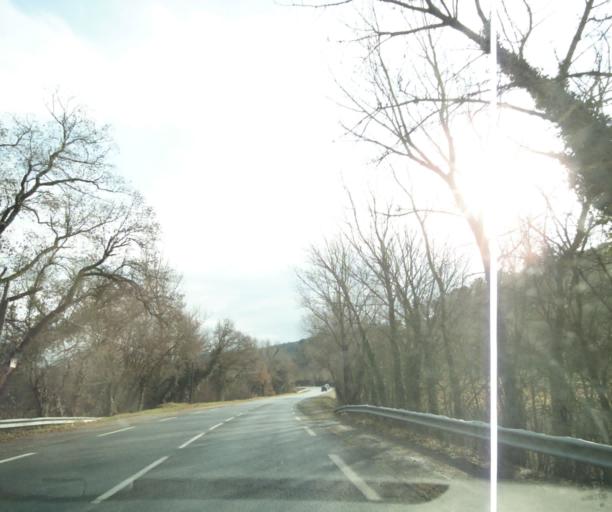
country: FR
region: Provence-Alpes-Cote d'Azur
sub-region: Departement du Var
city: Tourves
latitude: 43.4034
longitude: 5.9421
